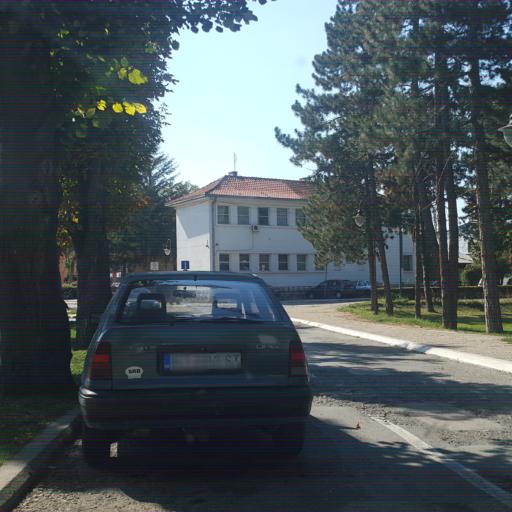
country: RS
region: Central Serbia
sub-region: Zajecarski Okrug
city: Knjazevac
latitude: 43.5691
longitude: 22.2551
